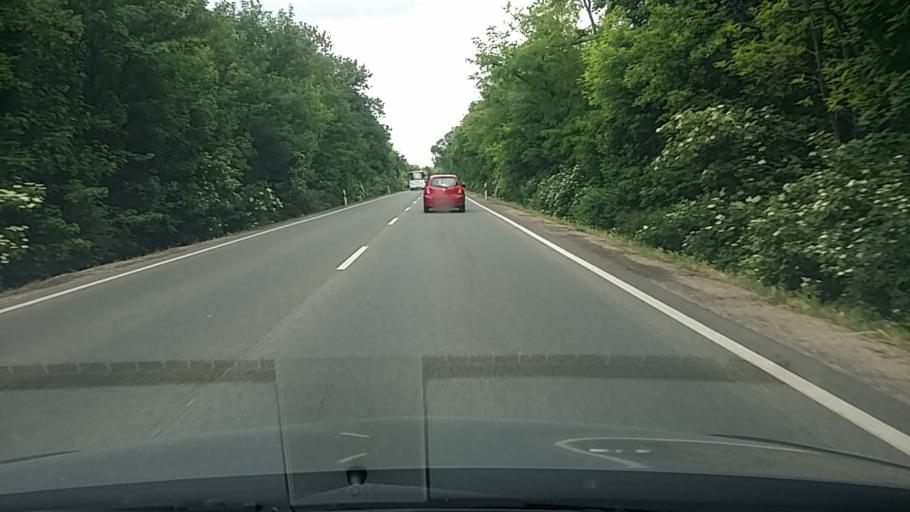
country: HU
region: Fejer
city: dunaujvaros
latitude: 46.9646
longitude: 18.9084
